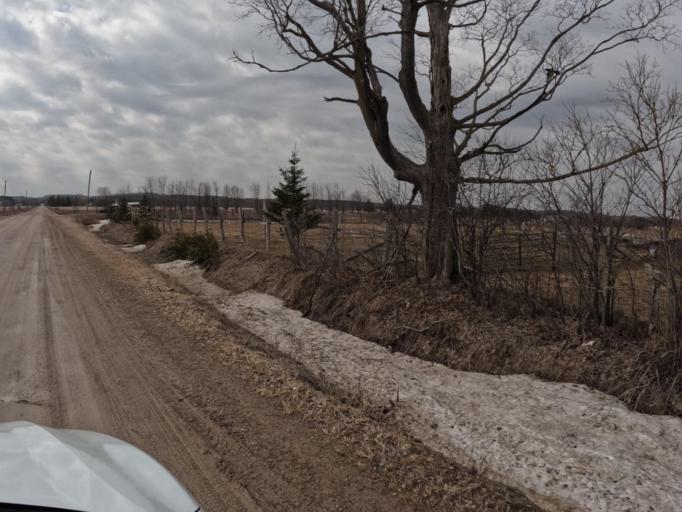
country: CA
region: Ontario
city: Orangeville
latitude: 43.9080
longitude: -80.2150
